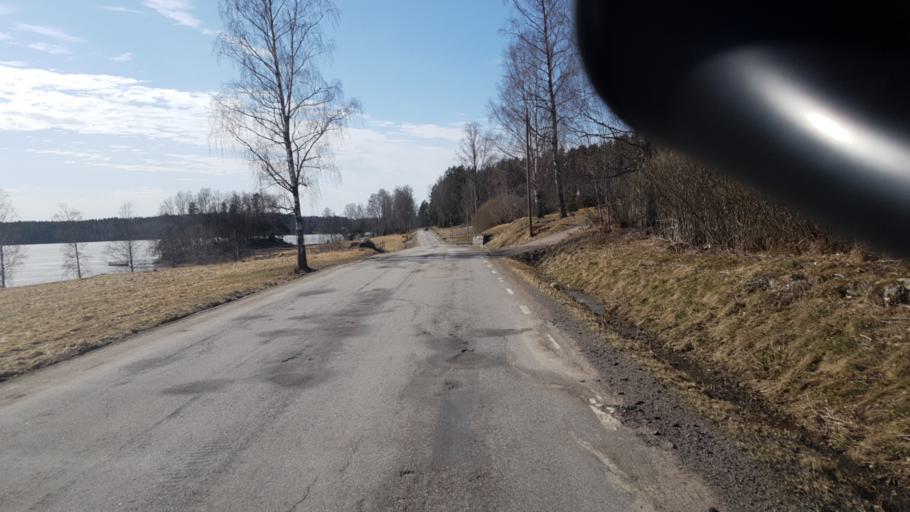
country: SE
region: Vaermland
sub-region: Arvika Kommun
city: Arvika
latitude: 59.6615
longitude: 12.7074
